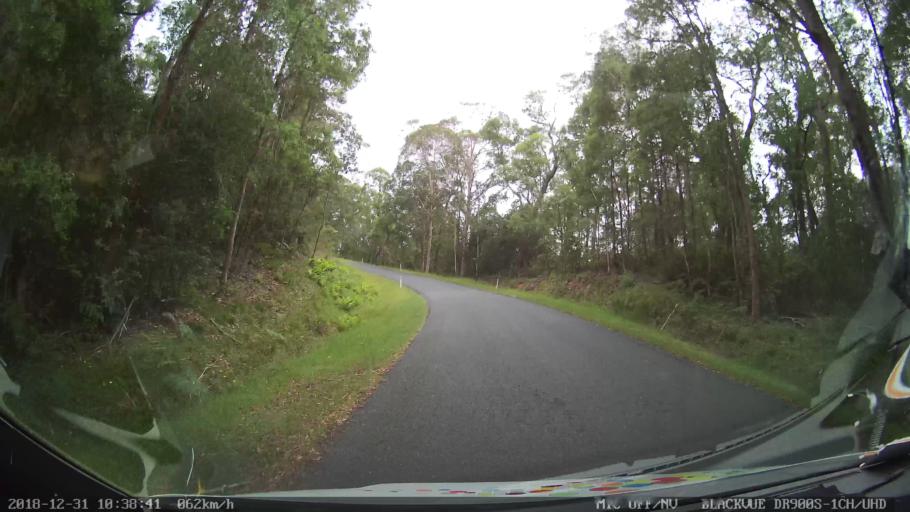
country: AU
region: New South Wales
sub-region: Snowy River
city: Jindabyne
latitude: -36.4051
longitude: 148.1777
